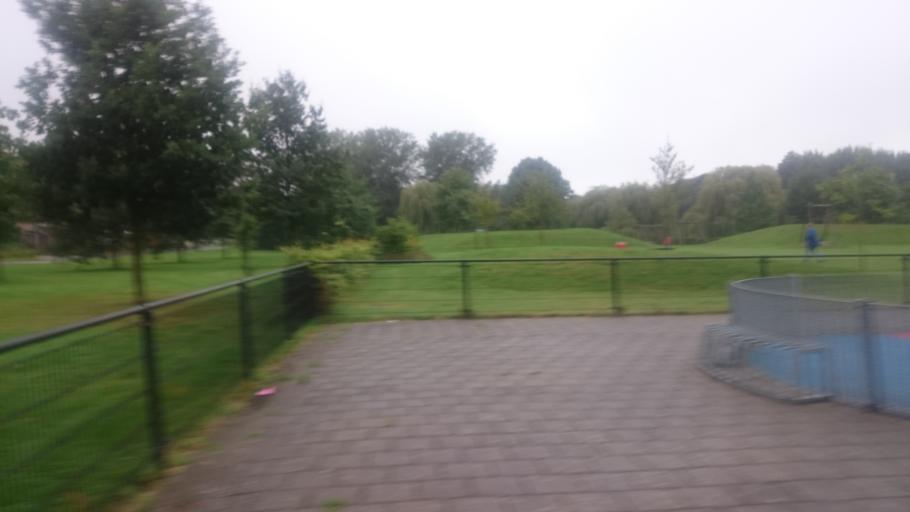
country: NL
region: Flevoland
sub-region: Gemeente Almere
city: Almere Stad
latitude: 52.3687
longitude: 5.2087
